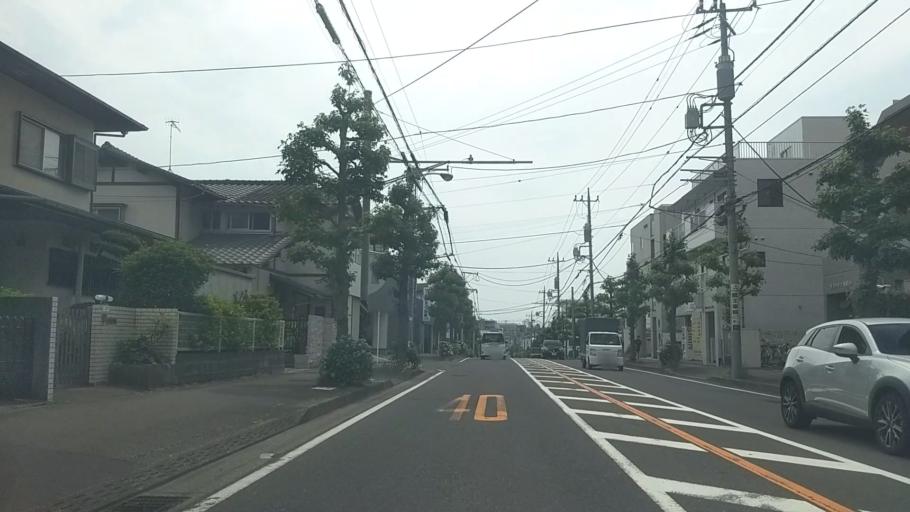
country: JP
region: Kanagawa
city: Fujisawa
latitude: 35.3916
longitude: 139.4632
